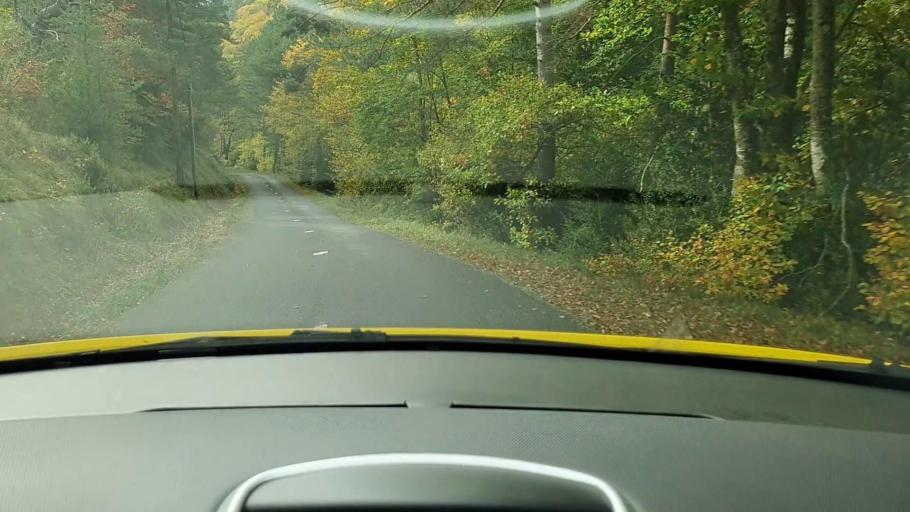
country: FR
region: Languedoc-Roussillon
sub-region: Departement de la Lozere
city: Meyrueis
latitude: 44.1197
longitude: 3.4332
